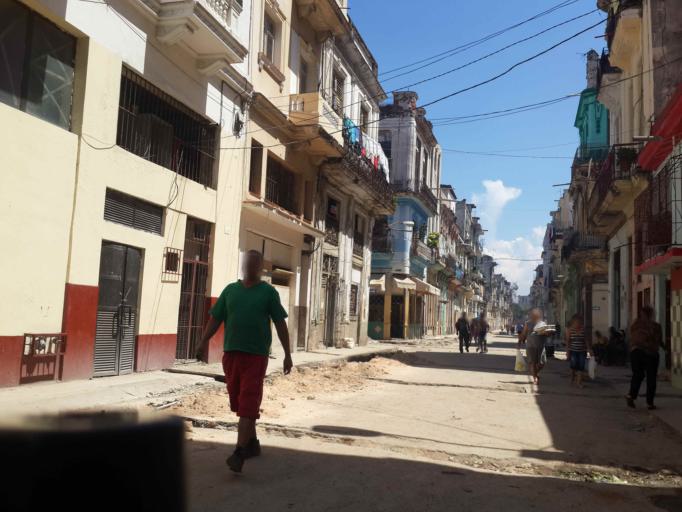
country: CU
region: La Habana
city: Centro Habana
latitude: 23.1402
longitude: -82.3634
